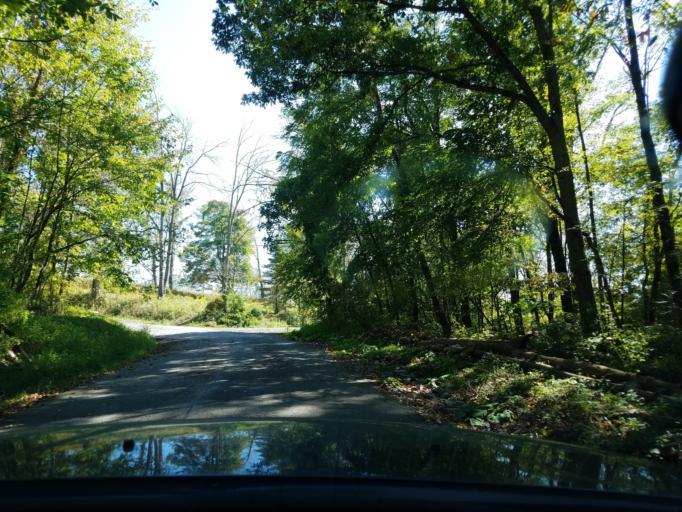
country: US
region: Pennsylvania
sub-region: Lawrence County
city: Ellwood City
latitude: 40.9327
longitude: -80.3115
